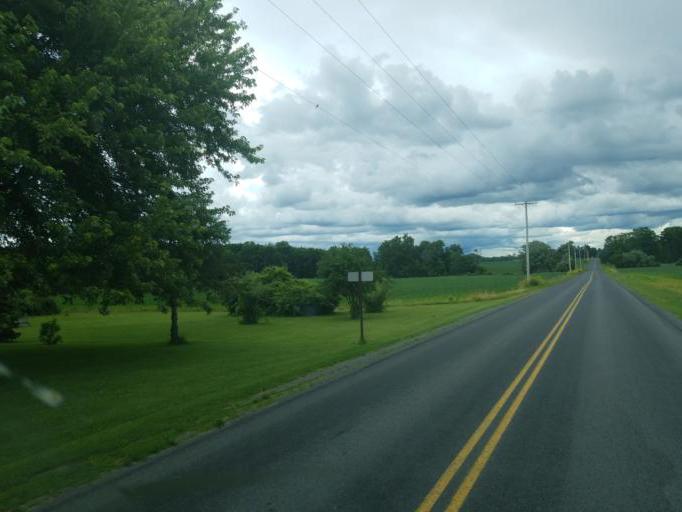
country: US
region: New York
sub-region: Ontario County
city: Geneva
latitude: 42.9625
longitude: -76.9516
